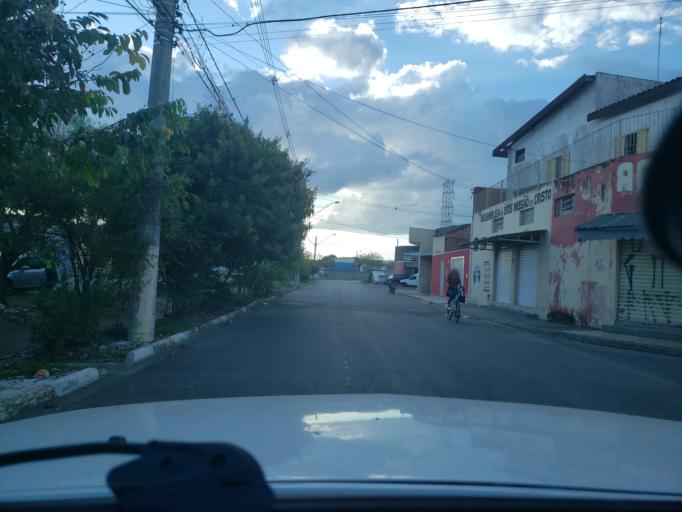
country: BR
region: Sao Paulo
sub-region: Moji-Guacu
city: Mogi-Gaucu
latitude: -22.3287
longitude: -46.9263
